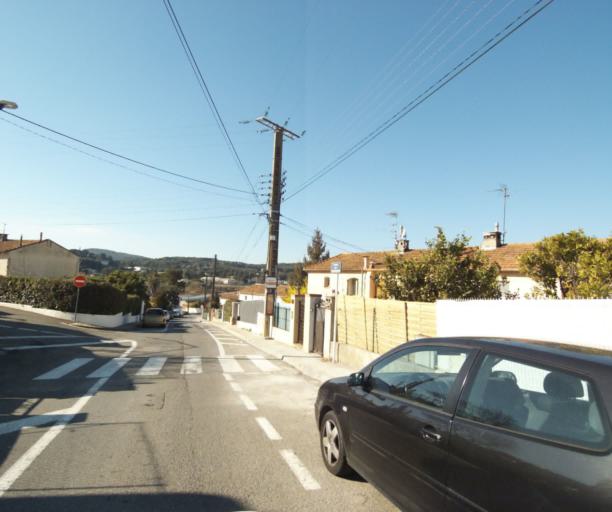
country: FR
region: Provence-Alpes-Cote d'Azur
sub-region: Departement des Alpes-Maritimes
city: Biot
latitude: 43.6067
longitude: 7.0845
